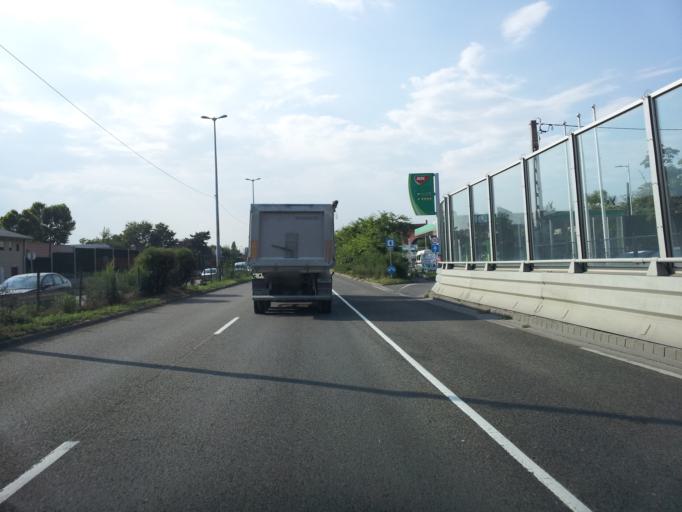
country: HU
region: Budapest
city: Budapest XIX. keruelet
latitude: 47.4421
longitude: 19.1332
